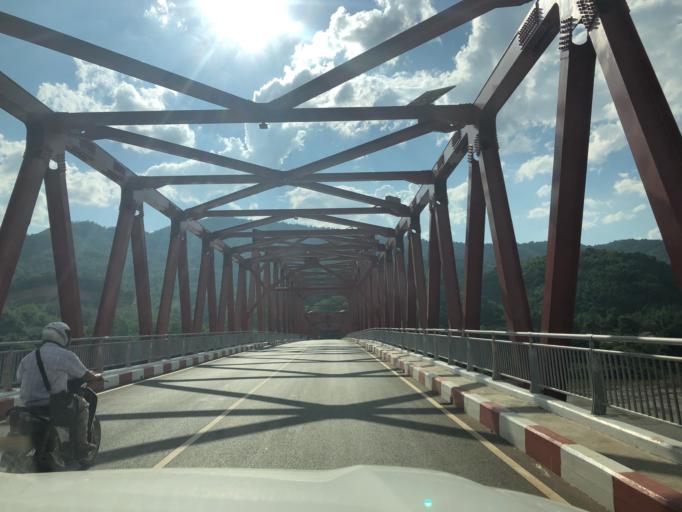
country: TH
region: Uttaradit
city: Ban Khok
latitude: 18.1758
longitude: 101.3936
